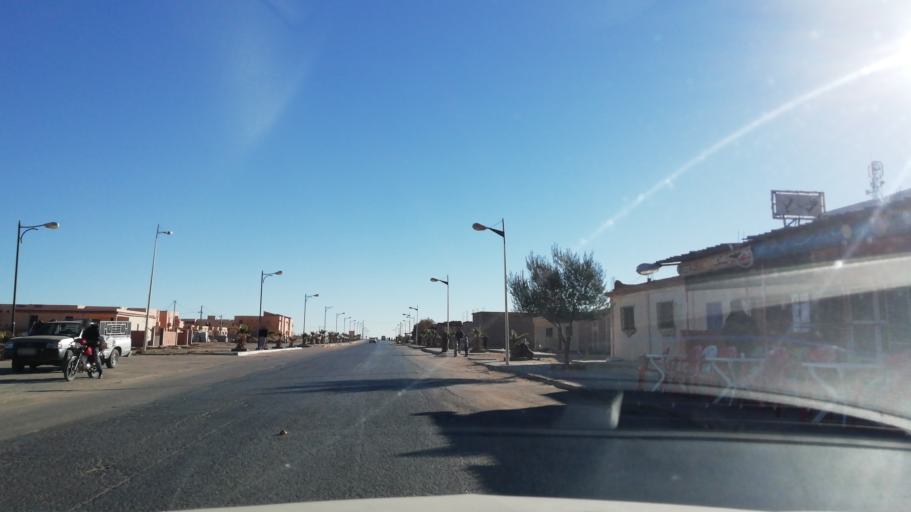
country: DZ
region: El Bayadh
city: El Bayadh
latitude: 33.8526
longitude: 0.6439
